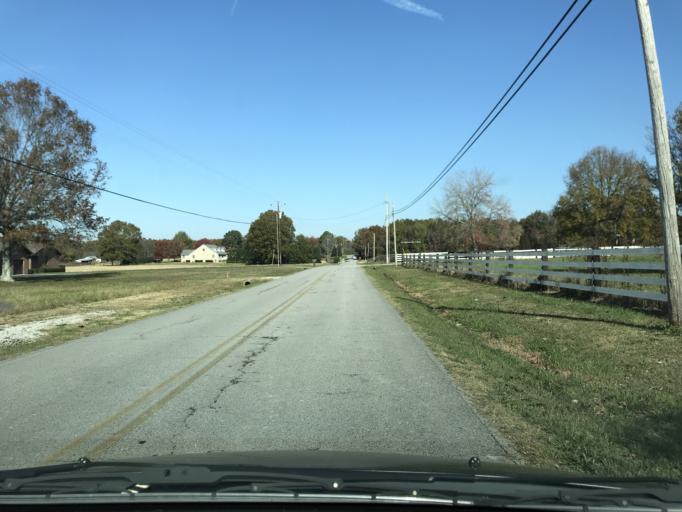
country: US
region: Tennessee
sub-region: Coffee County
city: Tullahoma
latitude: 35.3929
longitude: -86.1639
